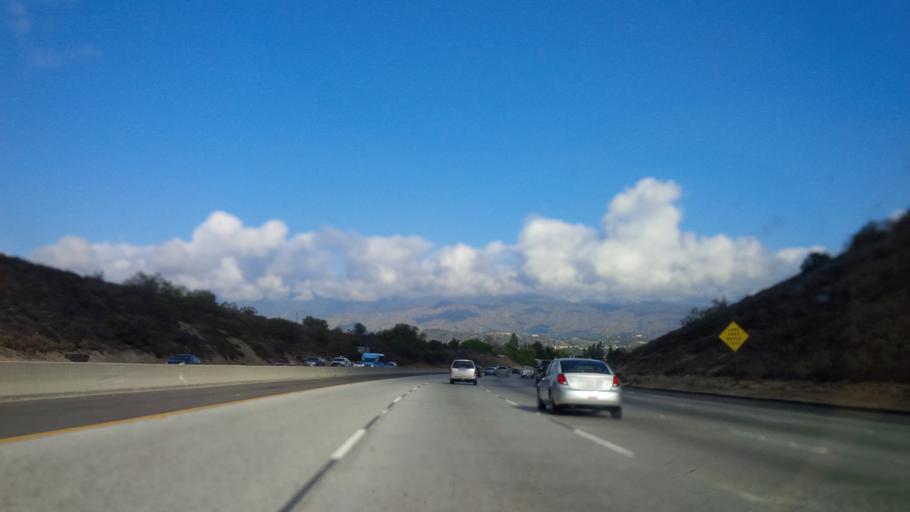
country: US
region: California
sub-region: Los Angeles County
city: San Dimas
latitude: 34.0823
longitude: -117.8180
